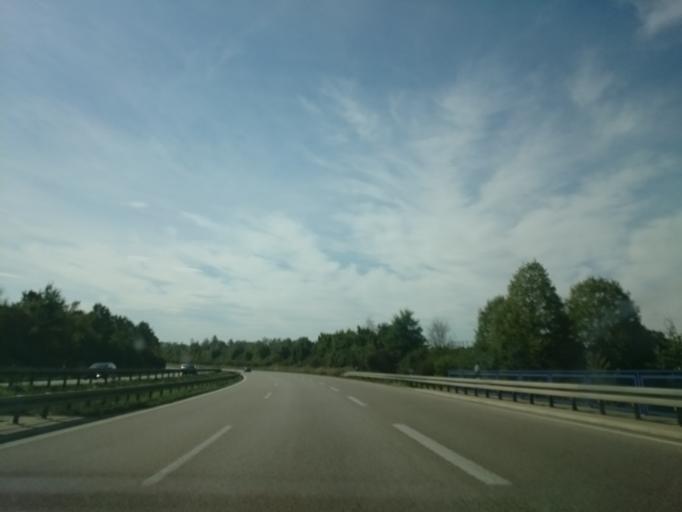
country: DE
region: Bavaria
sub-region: Swabia
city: Gersthofen
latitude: 48.4543
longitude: 10.8729
